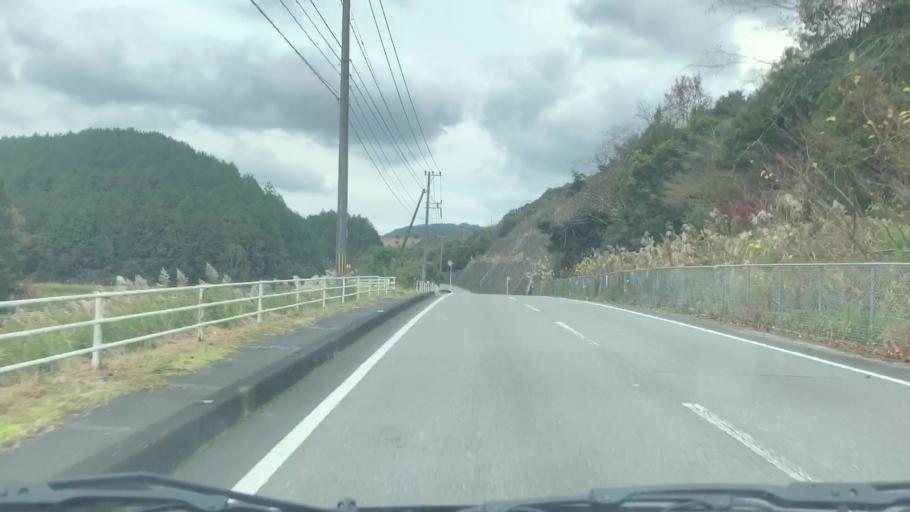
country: JP
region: Saga Prefecture
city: Ureshinomachi-shimojuku
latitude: 33.1159
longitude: 129.9767
